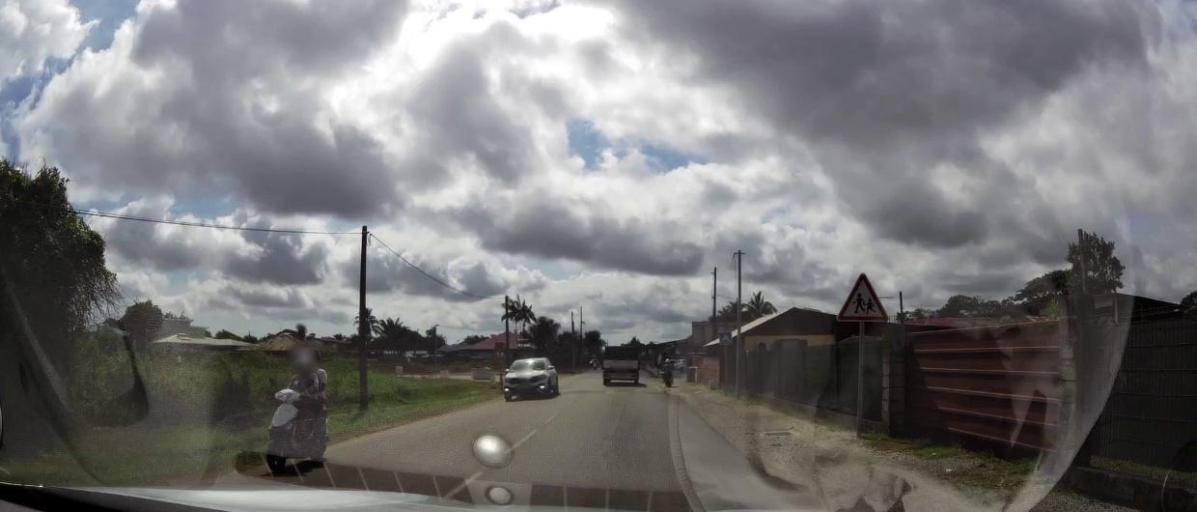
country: GF
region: Guyane
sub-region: Guyane
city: Matoury
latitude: 4.8745
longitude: -52.3310
